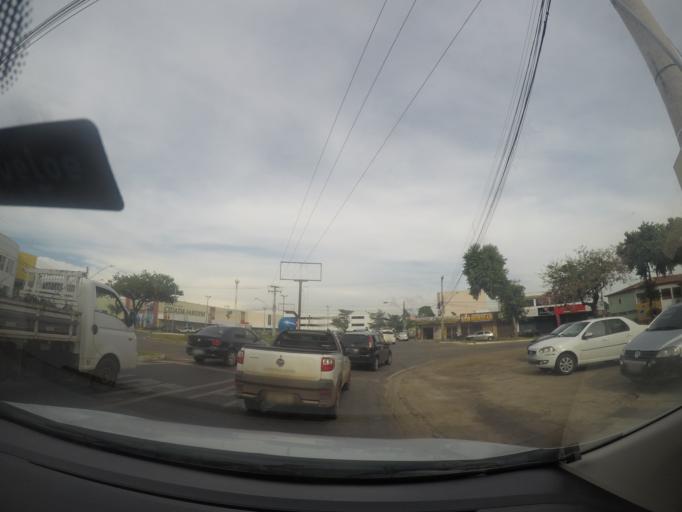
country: BR
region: Goias
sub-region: Goiania
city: Goiania
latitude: -16.6820
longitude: -49.3125
